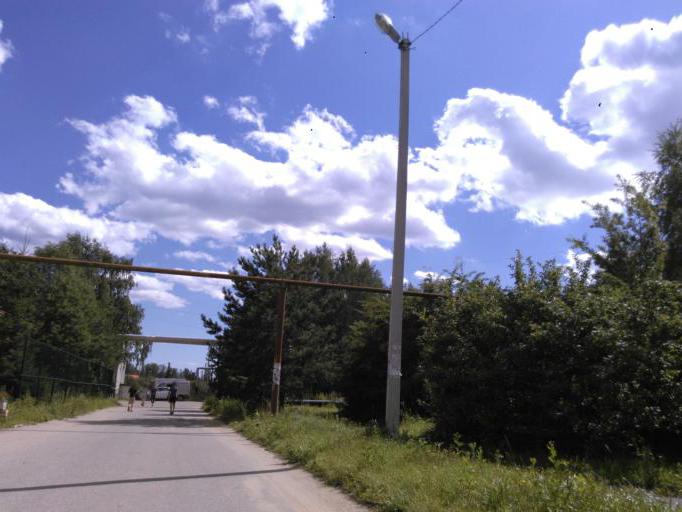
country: RU
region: Moskovskaya
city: Solnechnogorsk
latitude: 56.1413
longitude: 36.8940
